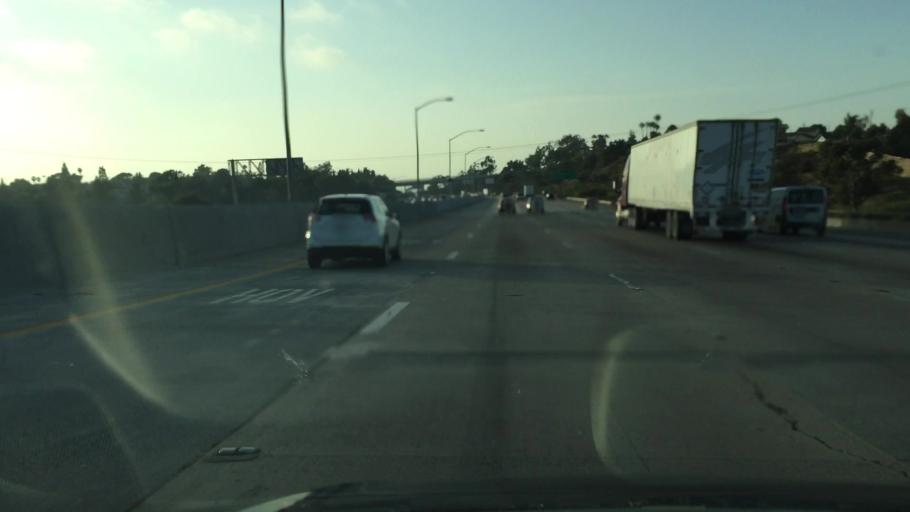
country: US
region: California
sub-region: San Diego County
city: Bonita
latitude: 32.6286
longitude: -117.0434
